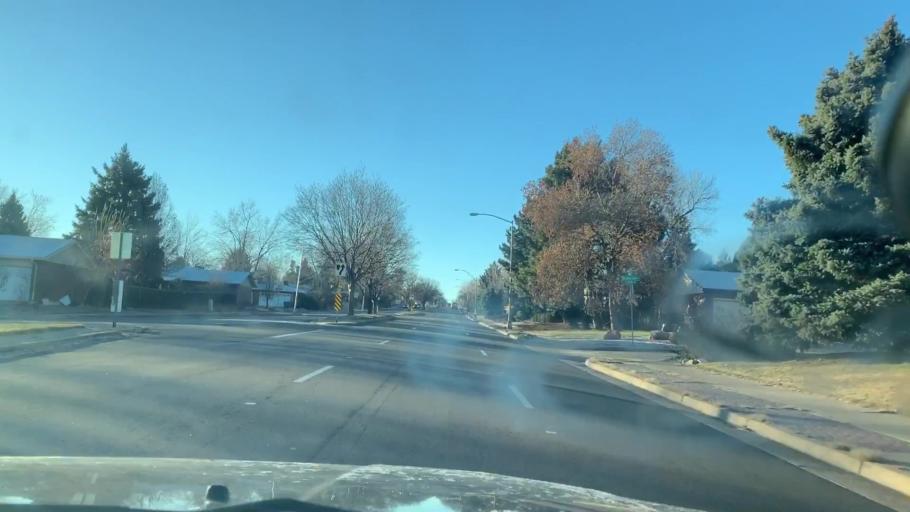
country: US
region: Colorado
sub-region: Arapahoe County
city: Glendale
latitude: 39.6725
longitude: -104.9130
